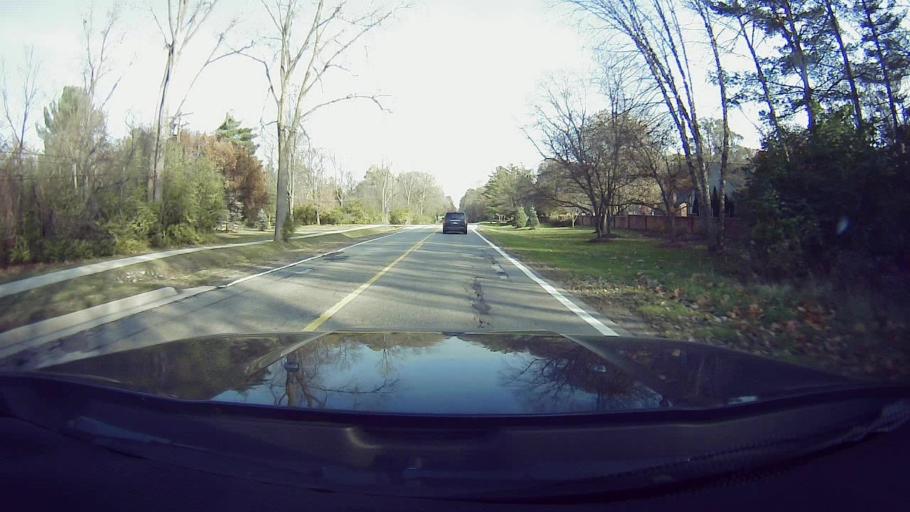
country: US
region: Michigan
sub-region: Oakland County
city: Bingham Farms
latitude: 42.5303
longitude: -83.2765
